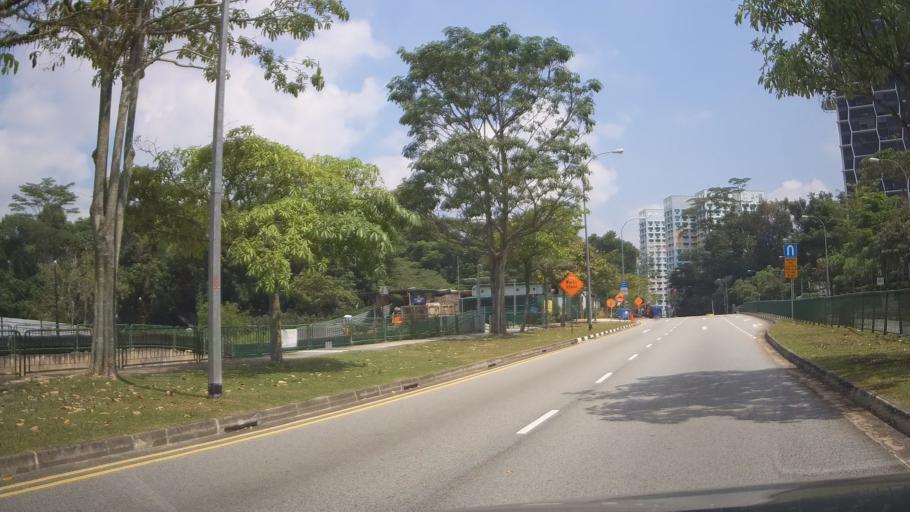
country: MY
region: Johor
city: Johor Bahru
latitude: 1.3687
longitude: 103.7754
